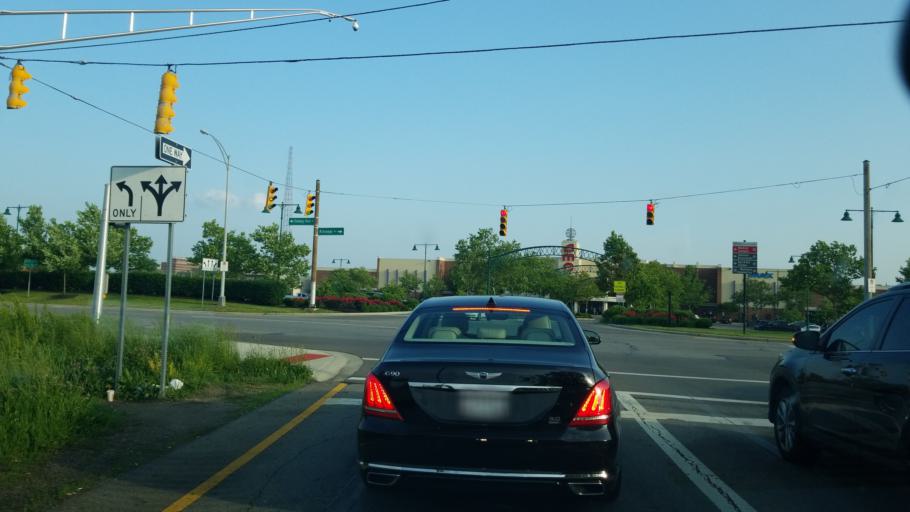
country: US
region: Ohio
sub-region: Franklin County
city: Grandview Heights
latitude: 39.9977
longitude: -83.0280
